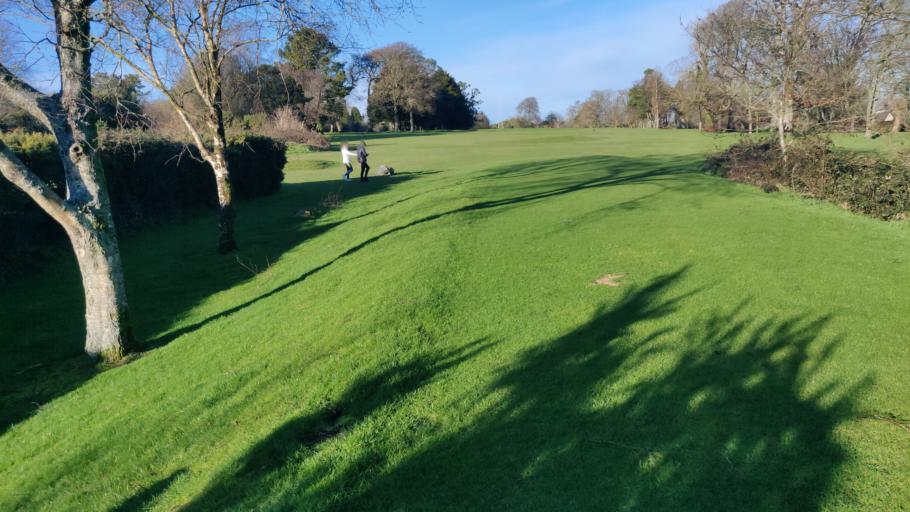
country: IE
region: Munster
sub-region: County Cork
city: Passage West
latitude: 51.8466
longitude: -8.3436
